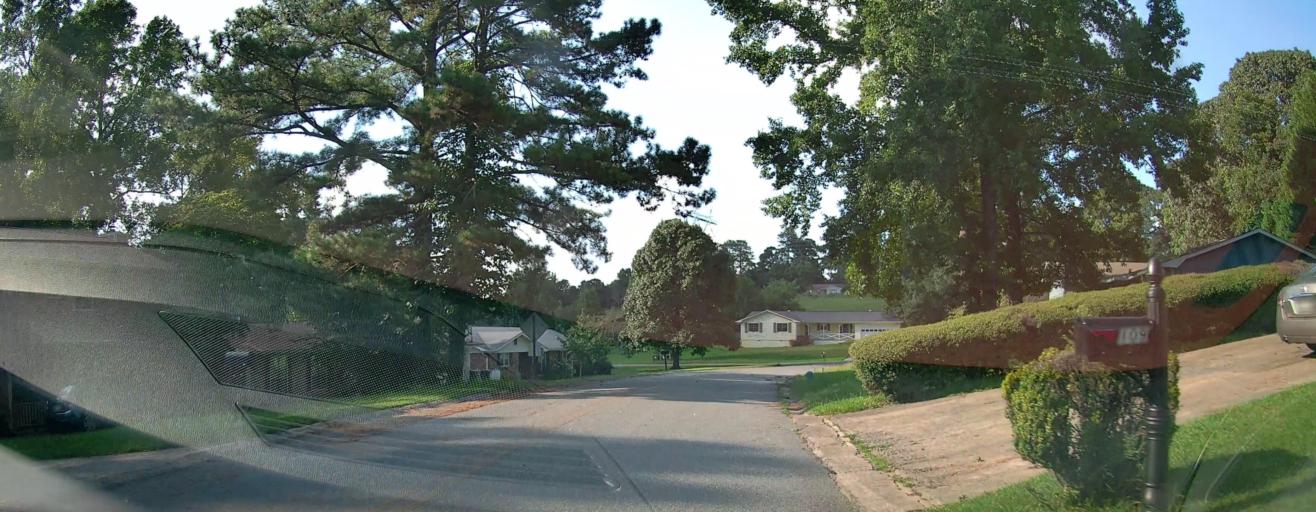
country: US
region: Georgia
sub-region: Houston County
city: Warner Robins
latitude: 32.5840
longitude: -83.6471
